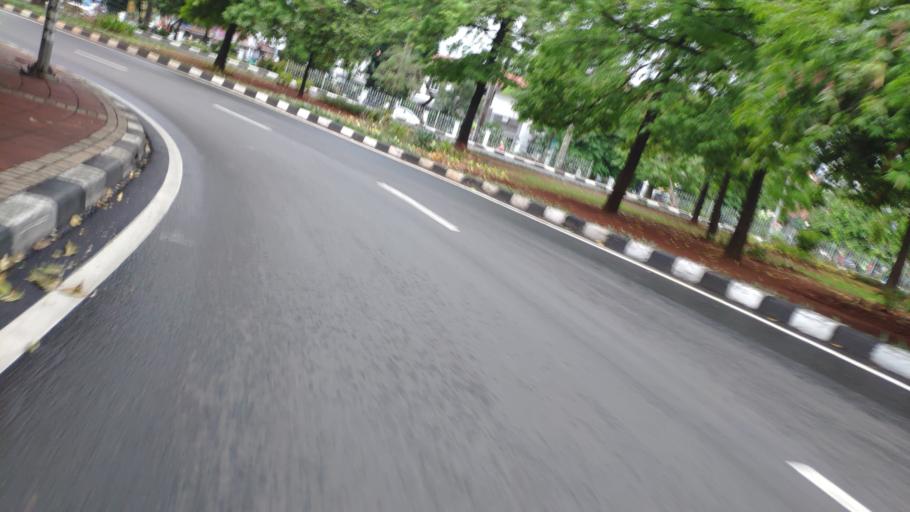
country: ID
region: Jakarta Raya
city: Jakarta
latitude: -6.2171
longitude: 106.8748
